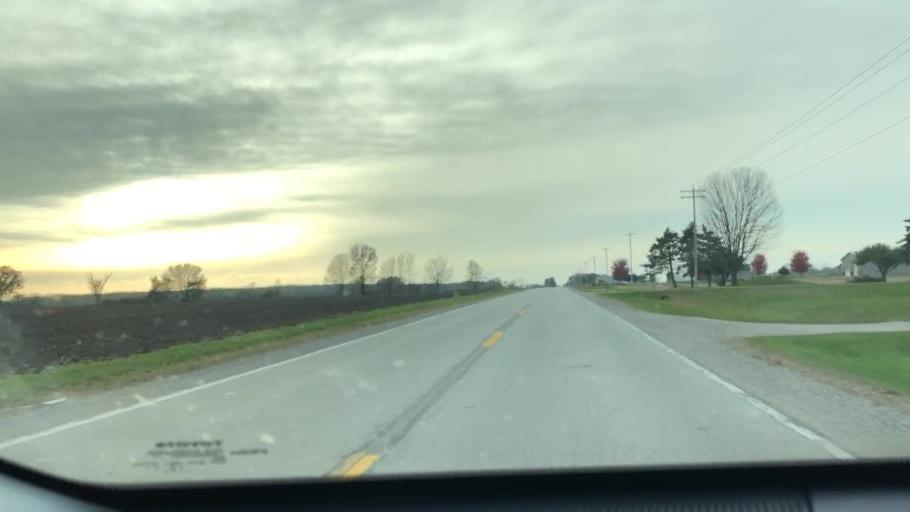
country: US
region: Wisconsin
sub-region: Outagamie County
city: Seymour
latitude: 44.4438
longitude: -88.3028
